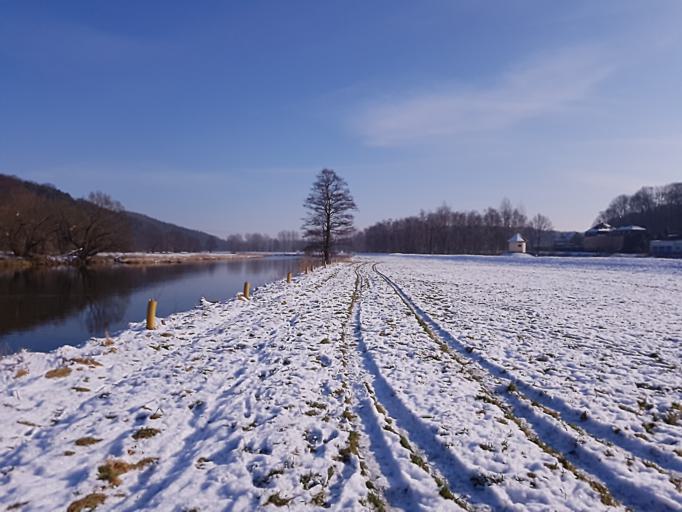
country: DE
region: Saxony
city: Leisnig
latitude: 51.1582
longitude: 12.9564
